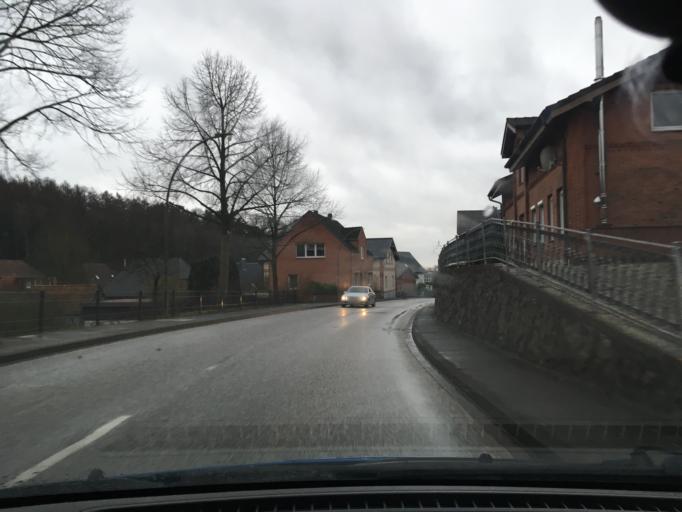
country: DE
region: Lower Saxony
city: Tespe
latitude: 53.4050
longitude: 10.4315
